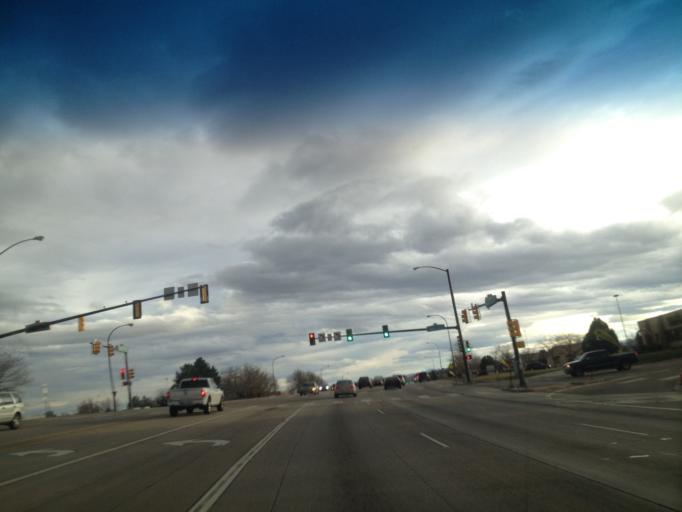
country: US
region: Colorado
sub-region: Adams County
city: Westminster
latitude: 39.8600
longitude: -105.0818
